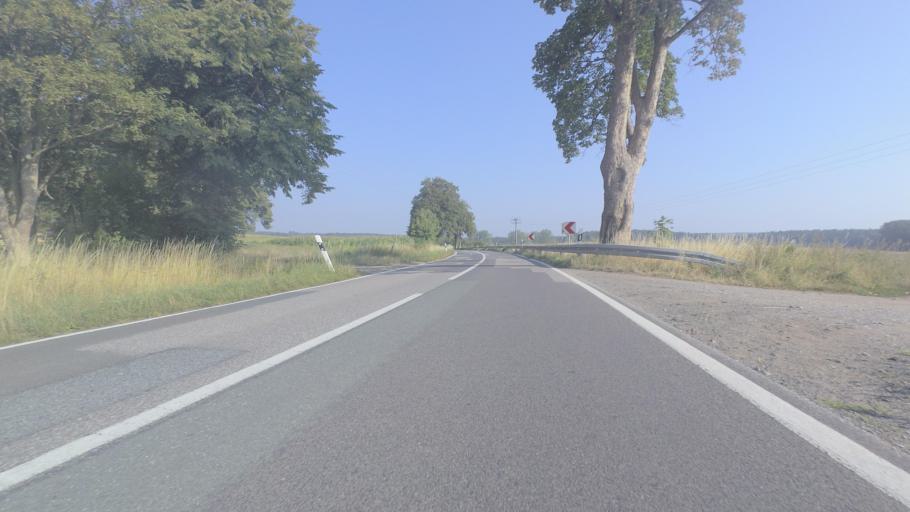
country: DE
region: Mecklenburg-Vorpommern
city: Malchow
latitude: 53.4379
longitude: 12.4350
